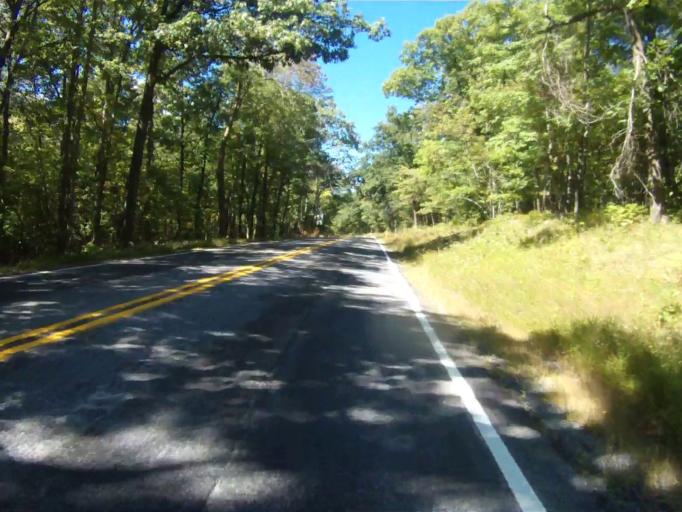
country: US
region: Pennsylvania
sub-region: Centre County
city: Park Forest Village
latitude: 40.9228
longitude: -77.9531
